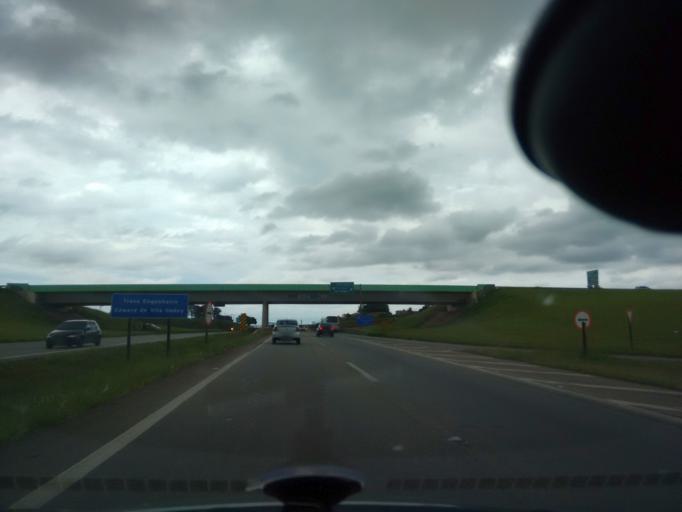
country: BR
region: Sao Paulo
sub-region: Indaiatuba
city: Indaiatuba
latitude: -23.0255
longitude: -47.1264
